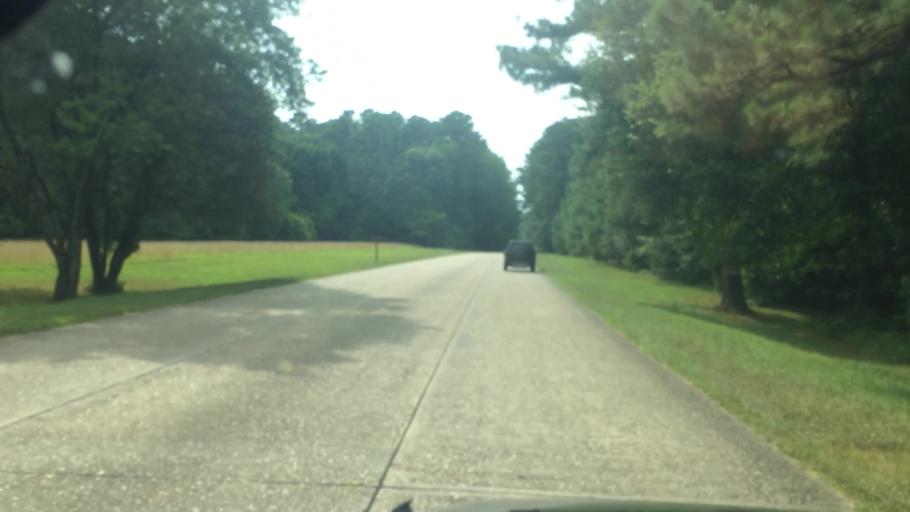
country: US
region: Virginia
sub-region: James City County
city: Williamsburg
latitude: 37.2176
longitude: -76.7595
